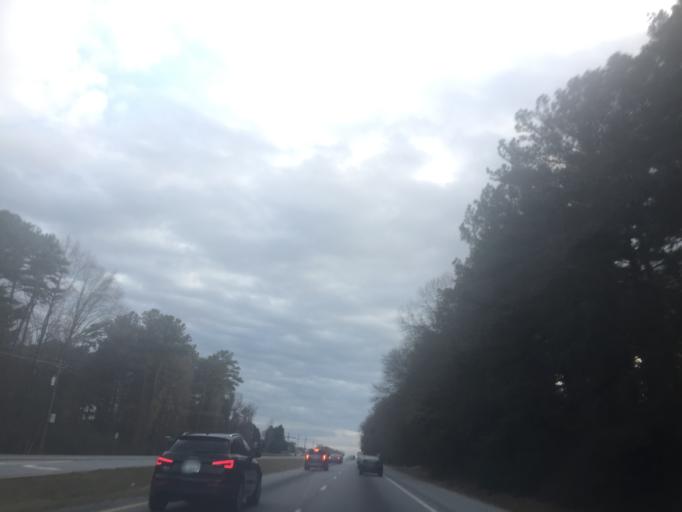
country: US
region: Georgia
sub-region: Clayton County
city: Riverdale
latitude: 33.6001
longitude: -84.4061
